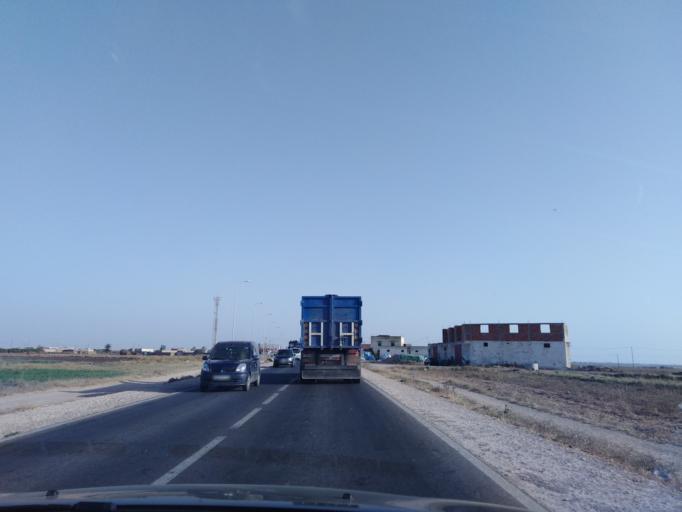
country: MA
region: Doukkala-Abda
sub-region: El-Jadida
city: Sidi Bennour
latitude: 32.5594
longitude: -8.7253
